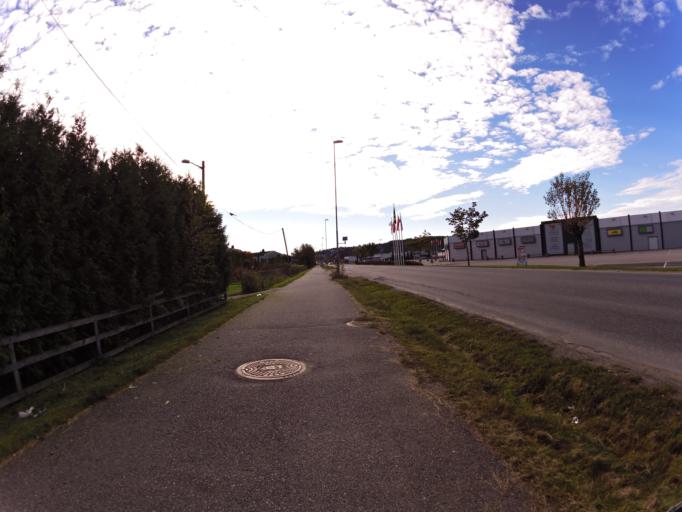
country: NO
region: Ostfold
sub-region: Sarpsborg
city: Sarpsborg
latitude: 59.2873
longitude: 11.0897
